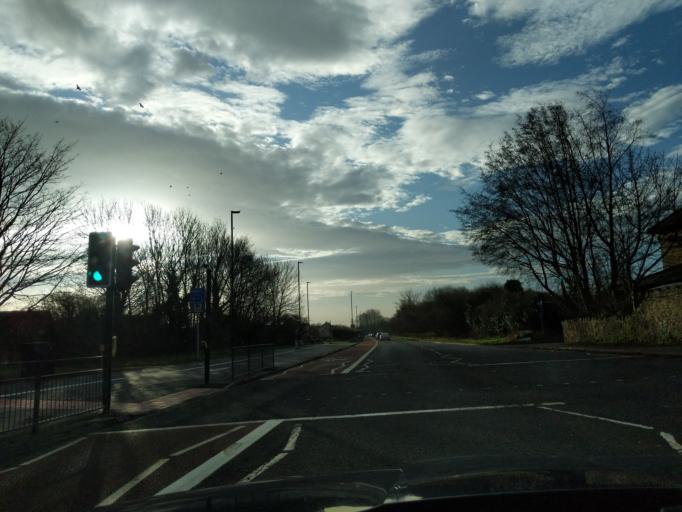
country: GB
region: England
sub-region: Newcastle upon Tyne
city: Gosforth
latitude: 55.0165
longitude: -1.5992
